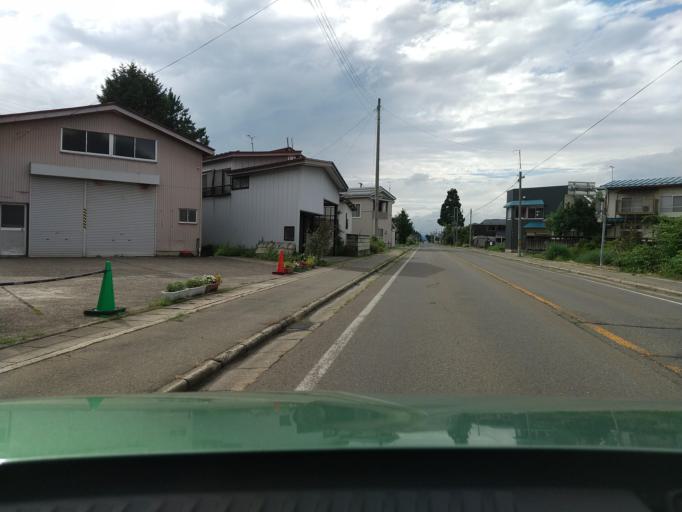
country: JP
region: Akita
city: Yuzawa
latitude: 39.2304
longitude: 140.5164
